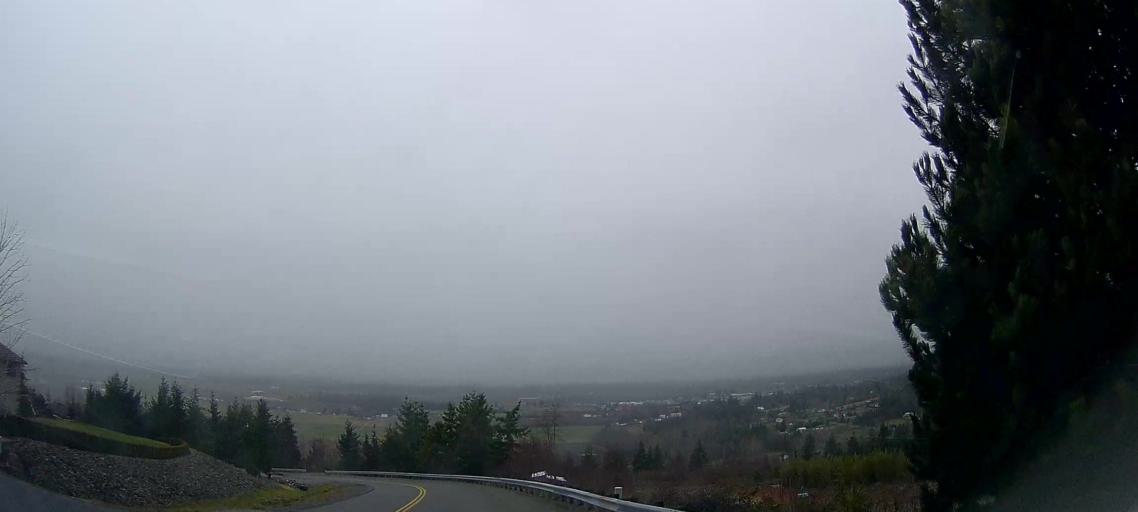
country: US
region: Washington
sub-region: Skagit County
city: Mount Vernon
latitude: 48.3787
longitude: -122.2974
